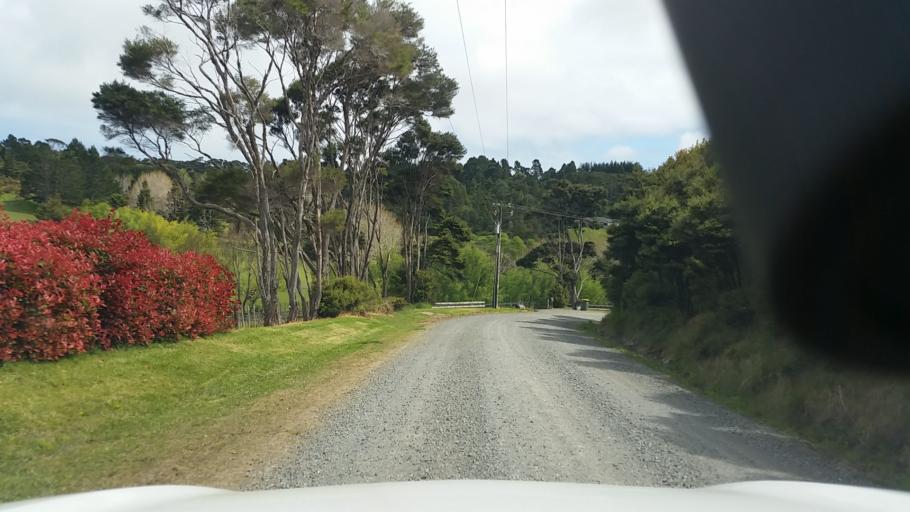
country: NZ
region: Auckland
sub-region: Auckland
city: Muriwai Beach
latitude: -36.8437
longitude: 174.5232
